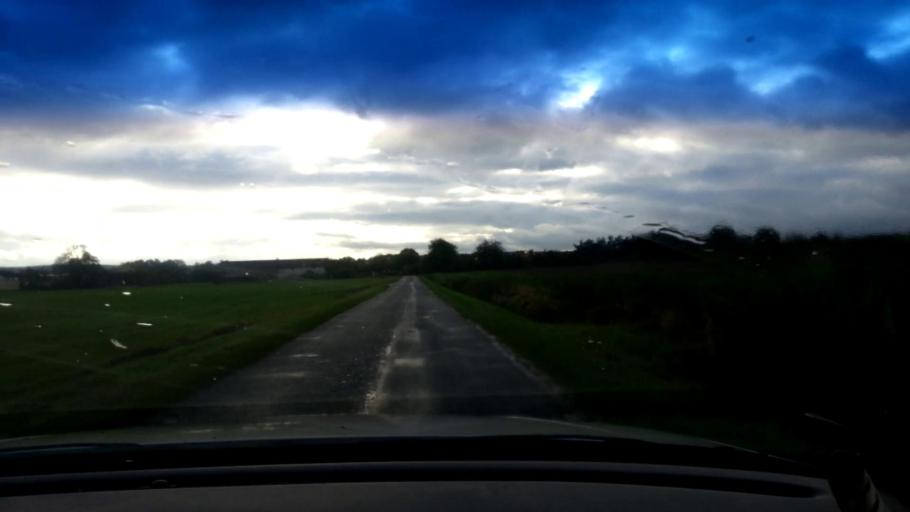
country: DE
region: Bavaria
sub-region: Upper Franconia
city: Burgebrach
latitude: 49.8279
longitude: 10.7099
